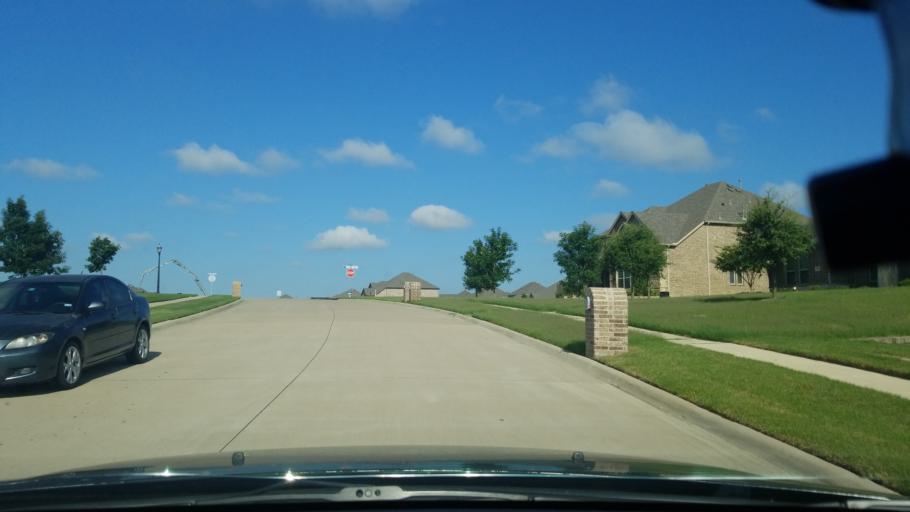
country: US
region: Texas
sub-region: Dallas County
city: Sunnyvale
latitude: 32.8080
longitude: -96.5691
